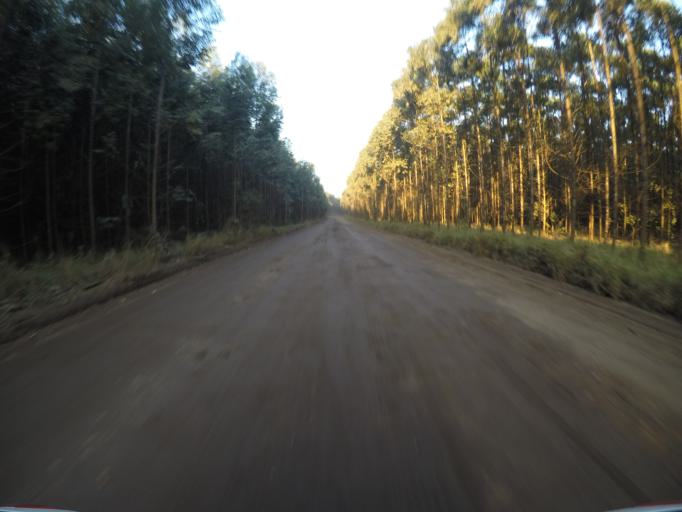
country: ZA
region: KwaZulu-Natal
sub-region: uThungulu District Municipality
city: KwaMbonambi
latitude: -28.6704
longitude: 32.0833
